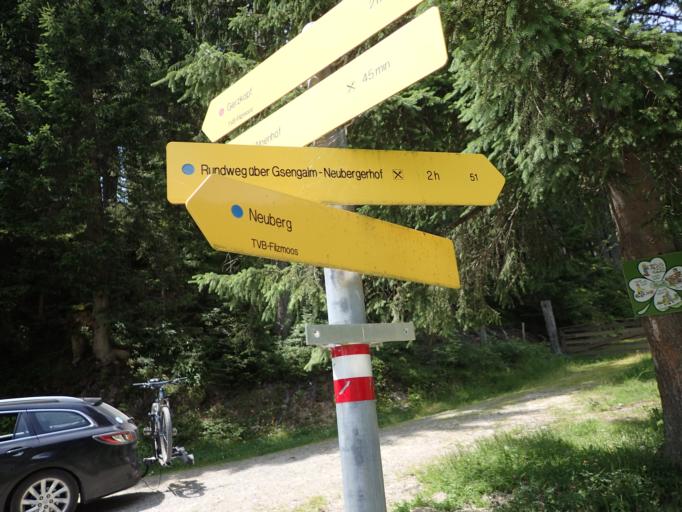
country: AT
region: Salzburg
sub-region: Politischer Bezirk Sankt Johann im Pongau
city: Filzmoos
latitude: 47.4545
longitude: 13.4537
